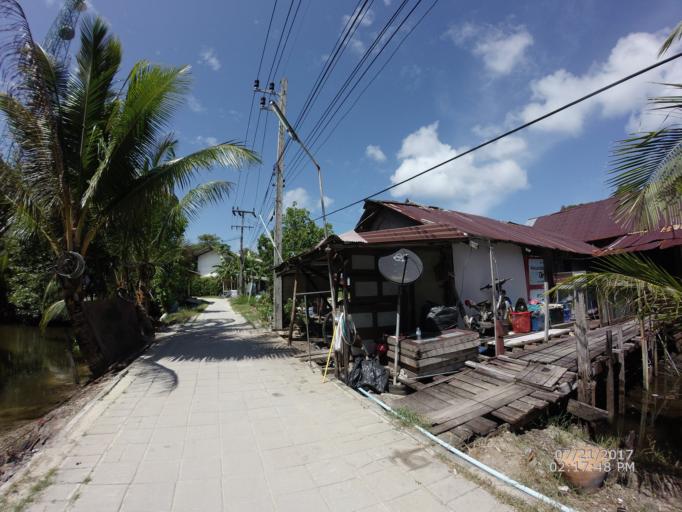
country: TH
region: Phangnga
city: Ban Phru Nai
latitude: 7.7587
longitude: 98.7706
